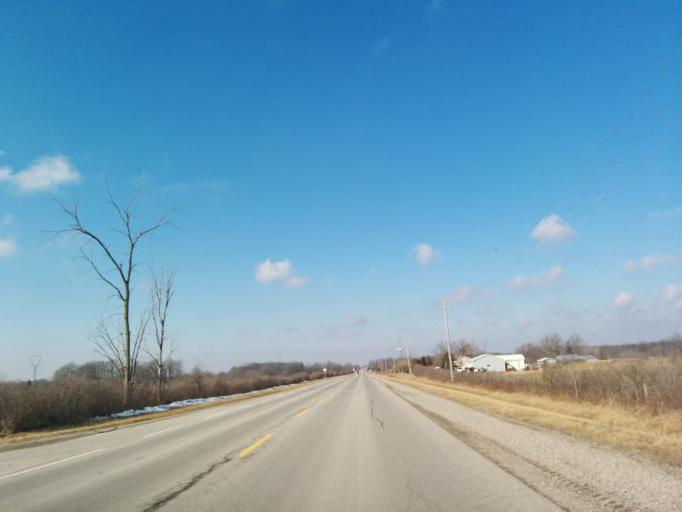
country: CA
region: Ontario
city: Brantford
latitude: 42.9953
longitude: -80.1421
